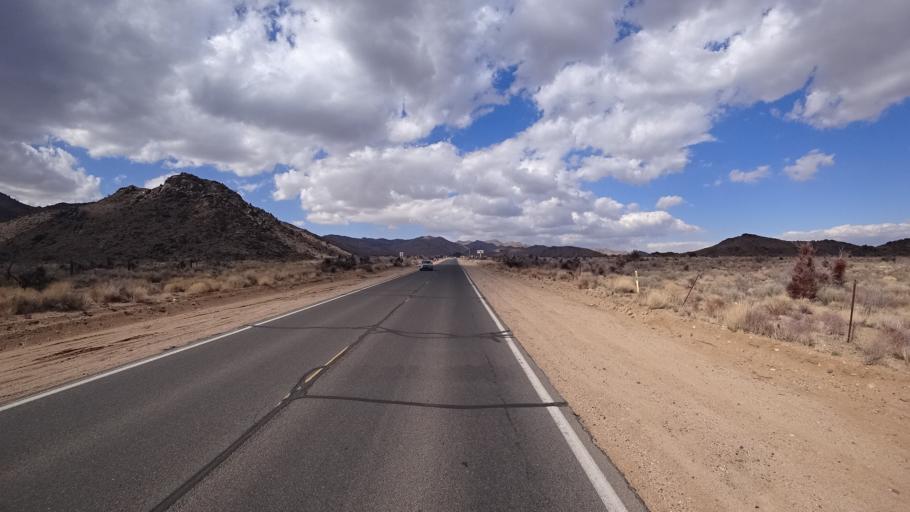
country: US
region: Arizona
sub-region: Mohave County
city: New Kingman-Butler
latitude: 35.2855
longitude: -114.0555
